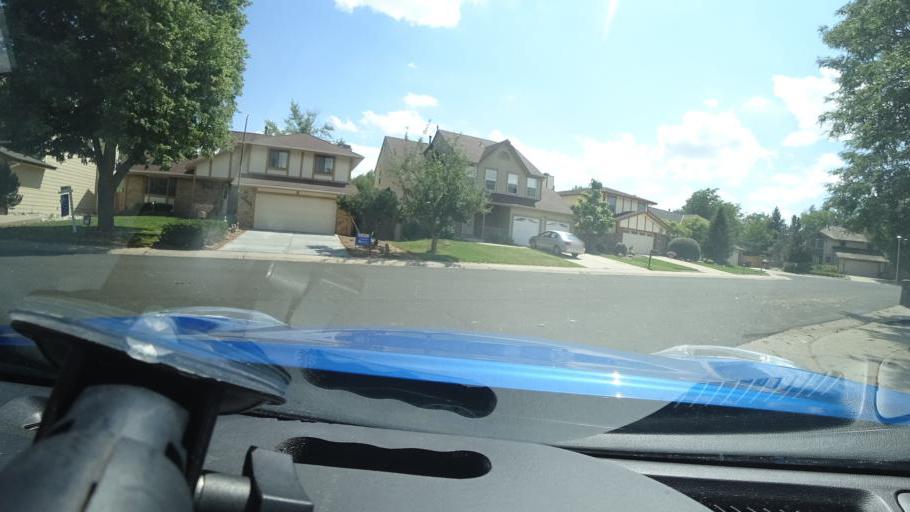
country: US
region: Colorado
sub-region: Adams County
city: Aurora
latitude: 39.6816
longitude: -104.8507
